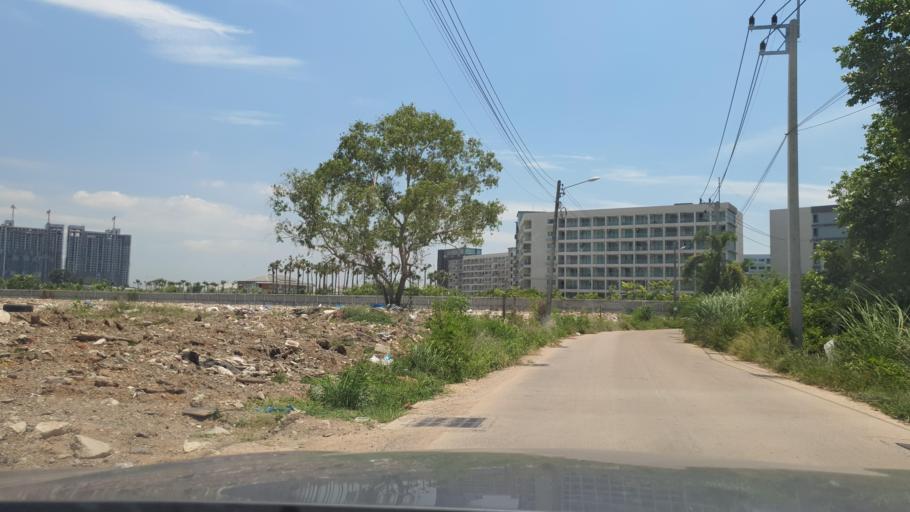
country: TH
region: Chon Buri
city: Phatthaya
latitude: 12.8974
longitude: 100.8829
